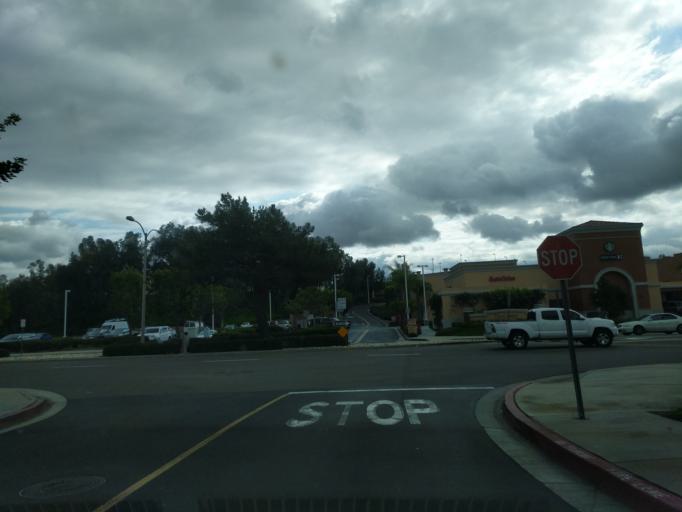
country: US
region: California
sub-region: Orange County
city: Laguna Niguel
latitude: 33.5566
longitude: -117.6863
